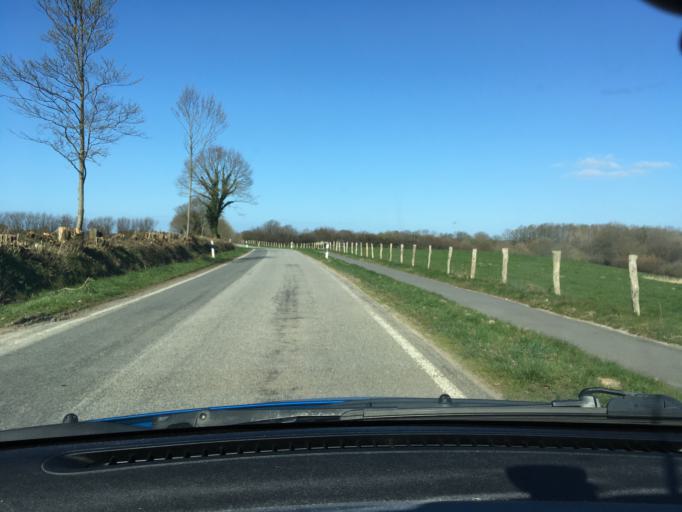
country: DE
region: Schleswig-Holstein
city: Borgwedel
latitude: 54.5014
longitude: 9.6433
